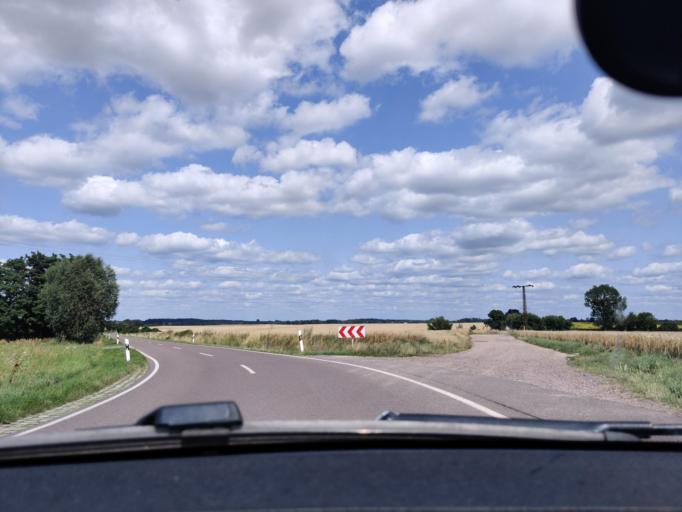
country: DE
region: Saxony-Anhalt
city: Leitzkau
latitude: 52.0602
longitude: 11.9662
